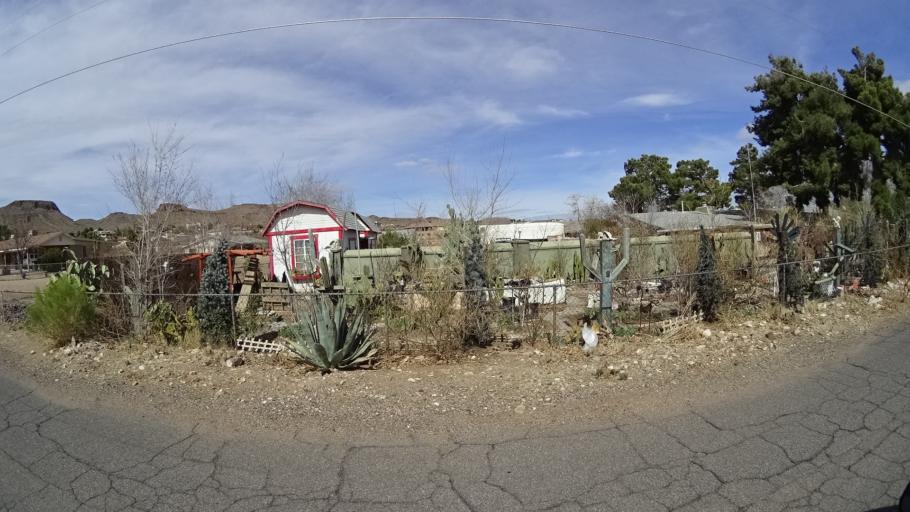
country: US
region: Arizona
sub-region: Mohave County
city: New Kingman-Butler
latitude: 35.2305
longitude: -114.0511
